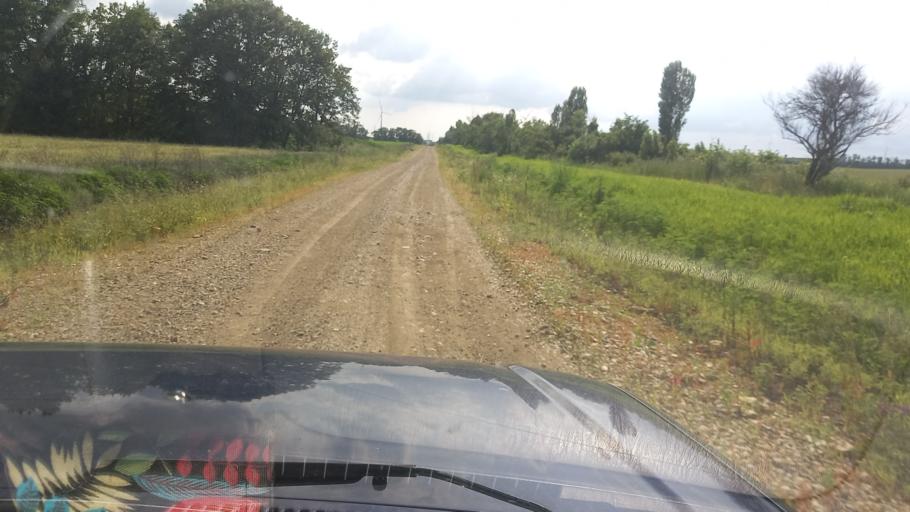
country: RU
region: Adygeya
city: Giaginskaya
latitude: 44.9482
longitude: 40.1248
